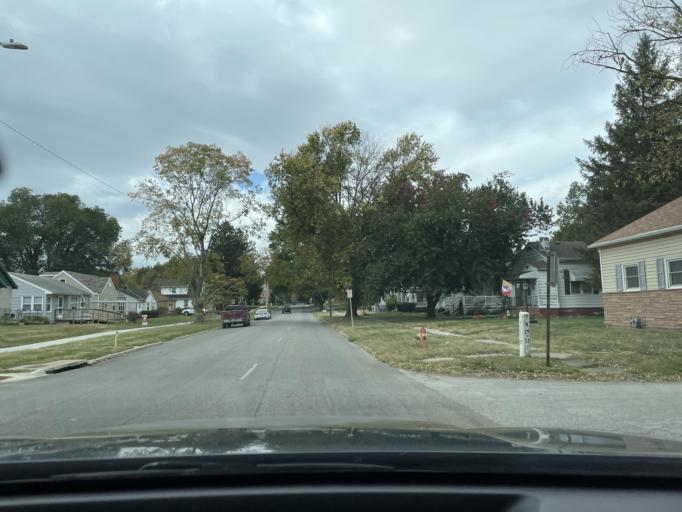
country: US
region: Missouri
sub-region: Buchanan County
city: Saint Joseph
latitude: 39.7692
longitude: -94.8222
